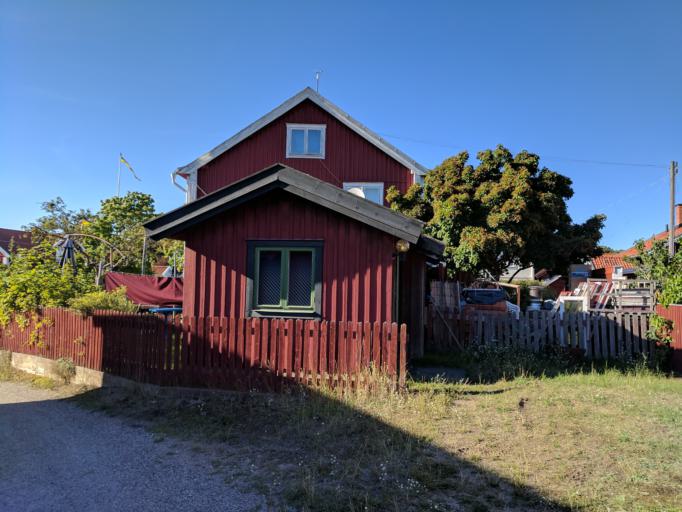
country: SE
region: Stockholm
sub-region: Varmdo Kommun
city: Holo
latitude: 59.2888
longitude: 18.9130
